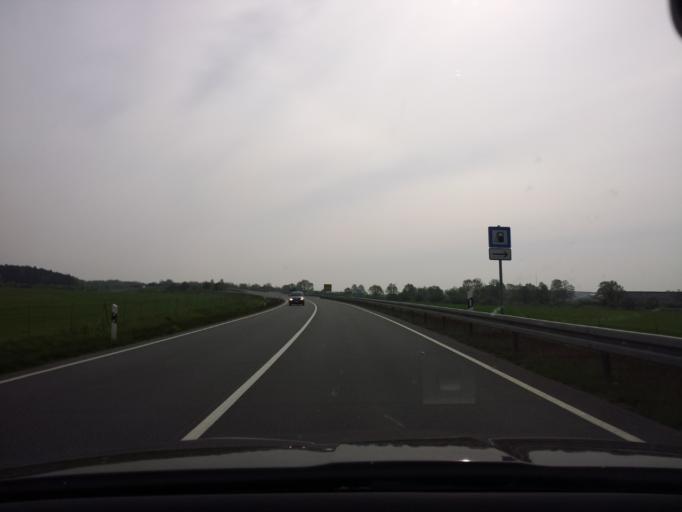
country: DE
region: Brandenburg
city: Luckau
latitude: 51.8632
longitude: 13.7274
